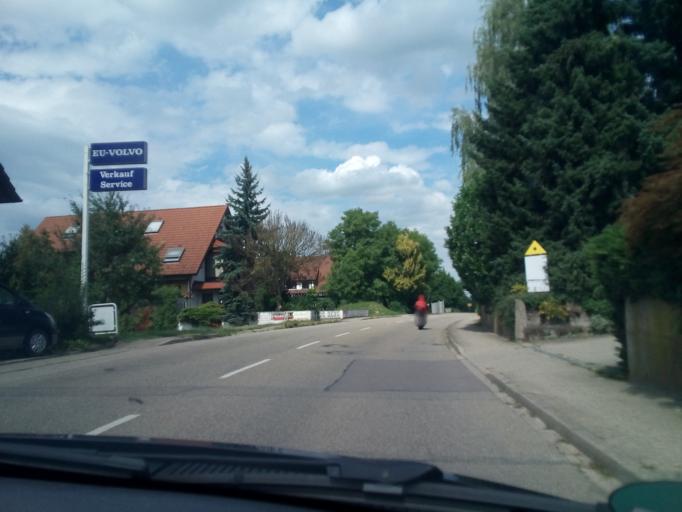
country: DE
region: Baden-Wuerttemberg
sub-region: Freiburg Region
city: Sasbach
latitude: 48.6424
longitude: 8.0932
